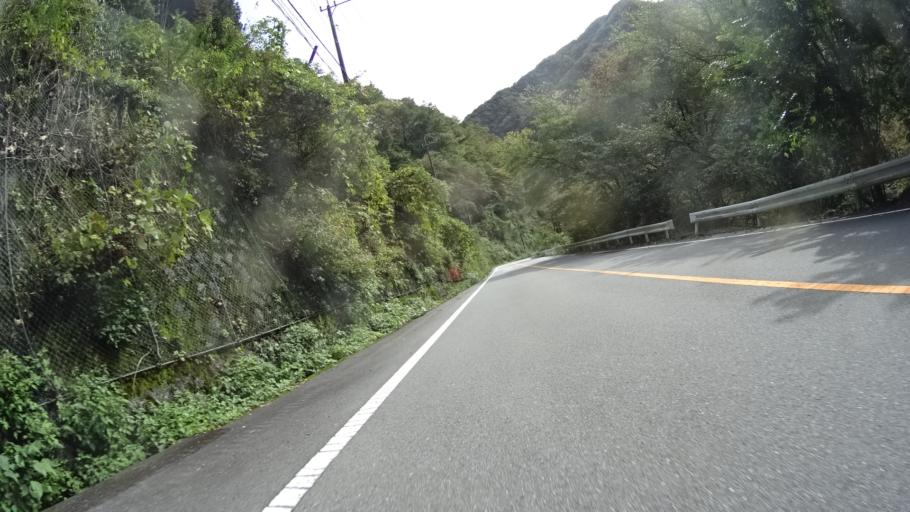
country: JP
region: Yamanashi
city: Otsuki
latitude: 35.7877
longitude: 138.9556
